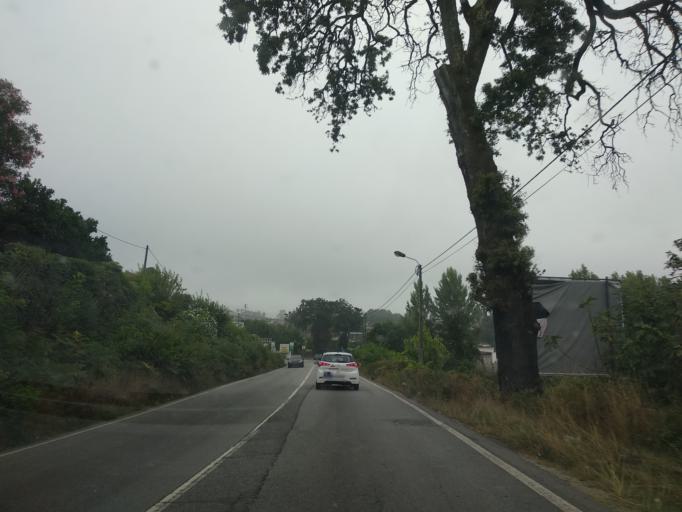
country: PT
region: Braga
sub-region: Vila Verde
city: Vila Verde
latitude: 41.6392
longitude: -8.4345
